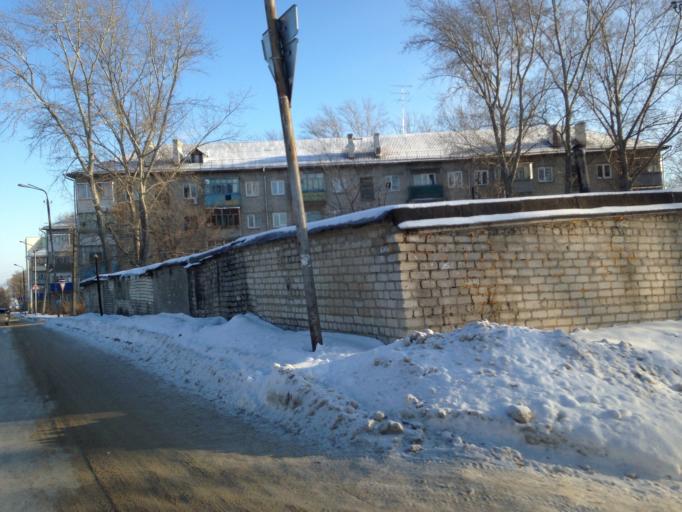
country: RU
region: Ulyanovsk
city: Novoul'yanovsk
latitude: 54.1532
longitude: 48.3796
